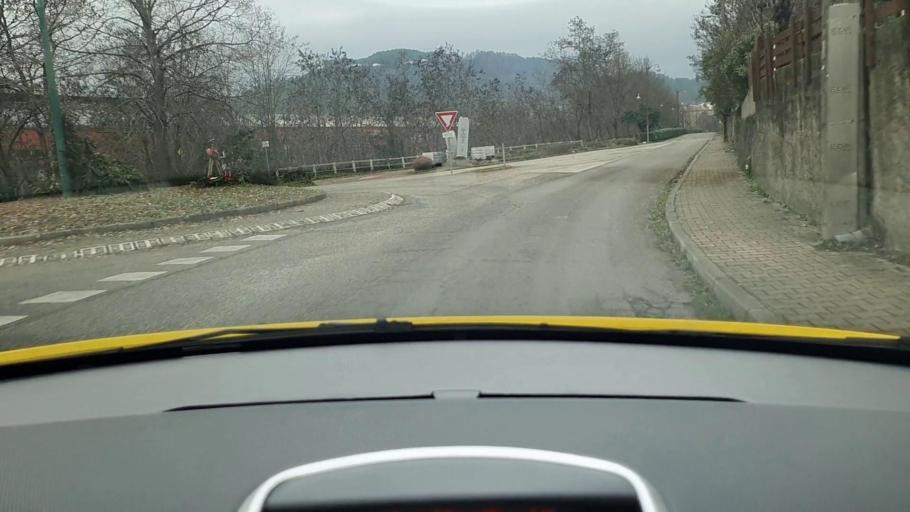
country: FR
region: Languedoc-Roussillon
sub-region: Departement du Gard
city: Besseges
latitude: 44.2939
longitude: 4.0938
